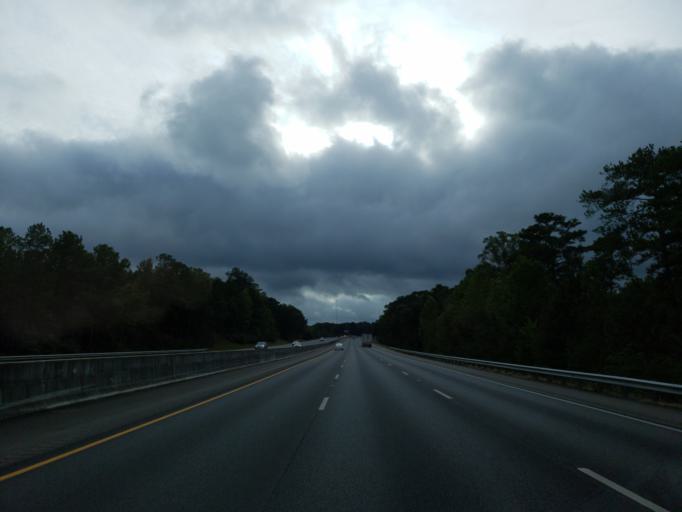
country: US
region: Alabama
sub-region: Bibb County
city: North Bibb
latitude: 33.2172
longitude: -87.1900
